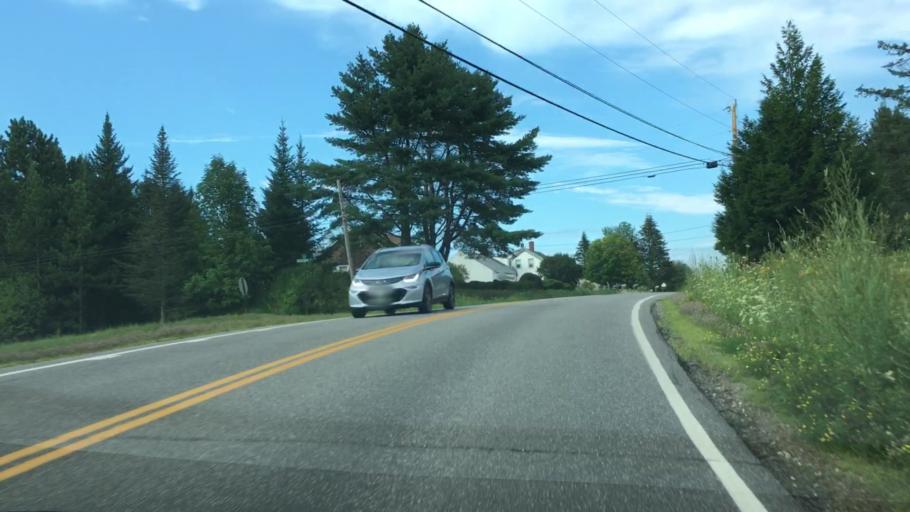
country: US
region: Maine
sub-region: Waldo County
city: Belfast
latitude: 44.4060
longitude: -69.0304
